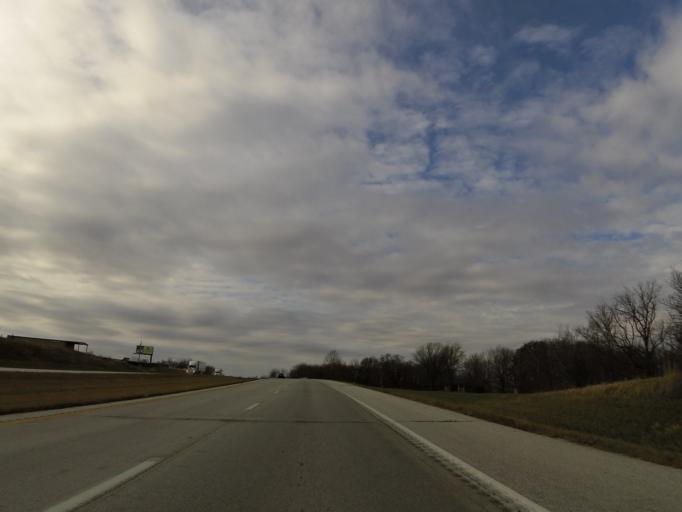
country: US
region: Missouri
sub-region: Marion County
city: Hannibal
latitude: 39.7415
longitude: -91.4199
